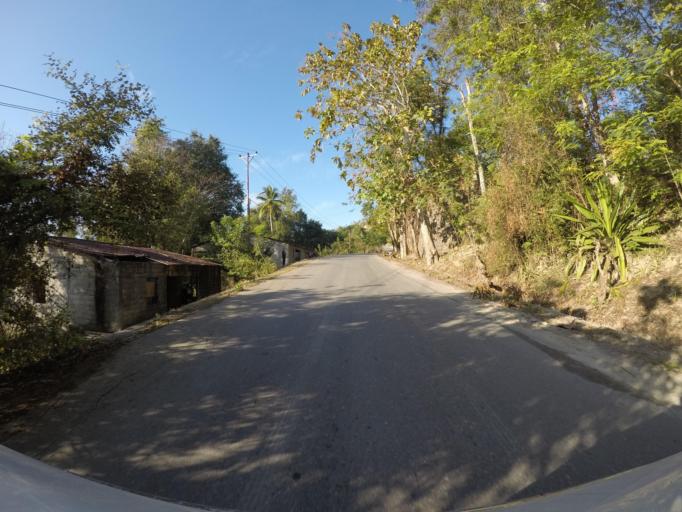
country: TL
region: Viqueque
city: Viqueque
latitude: -8.8702
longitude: 126.3617
